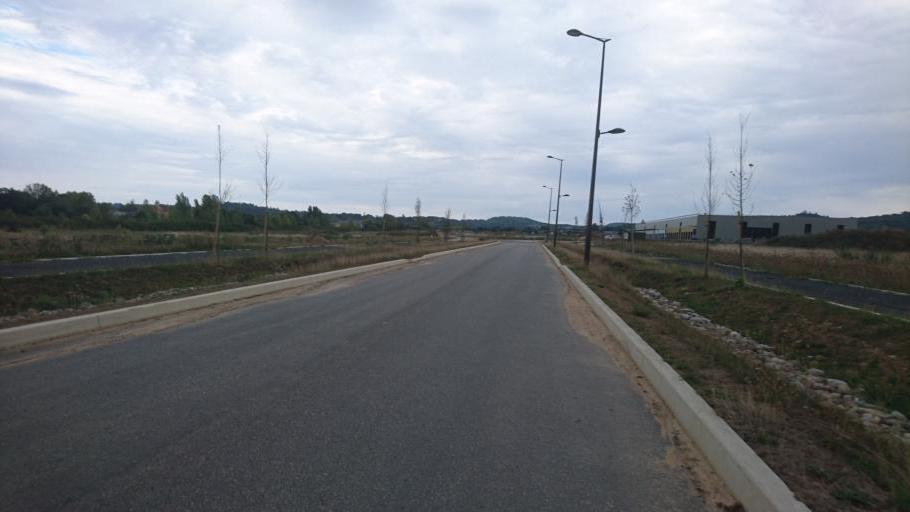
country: FR
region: Limousin
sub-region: Departement de la Correze
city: Saint-Pantaleon-de-Larche
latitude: 45.1511
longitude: 1.4720
